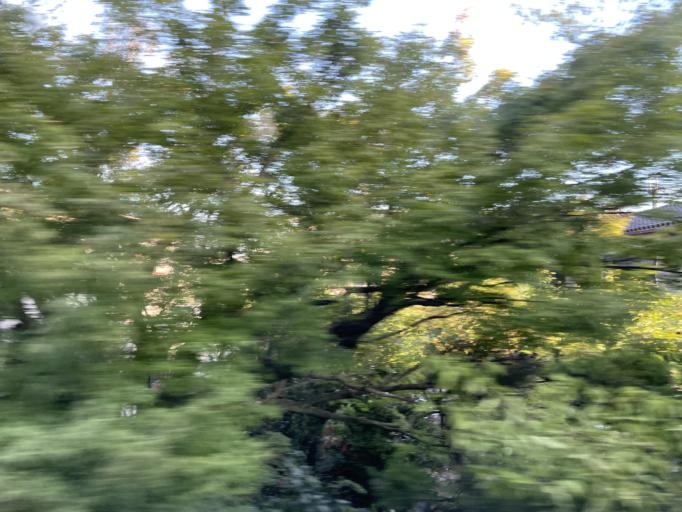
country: JP
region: Osaka
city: Kashihara
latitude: 34.5709
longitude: 135.6105
